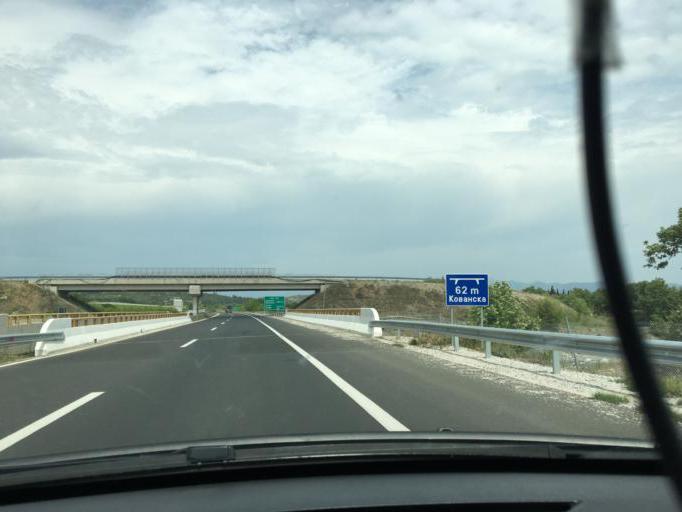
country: MK
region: Gevgelija
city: Gevgelija
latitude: 41.2114
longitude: 22.4941
